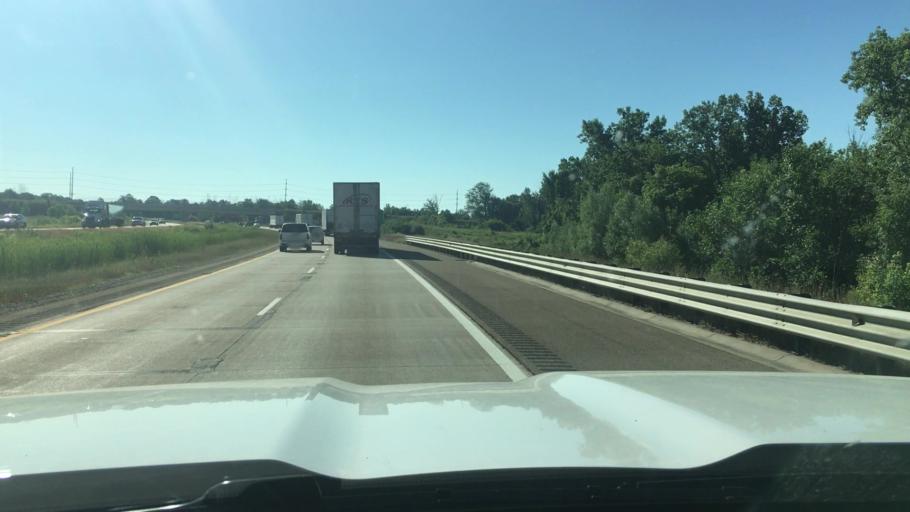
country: US
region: Michigan
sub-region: Kent County
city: Kentwood
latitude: 42.8472
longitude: -85.5709
